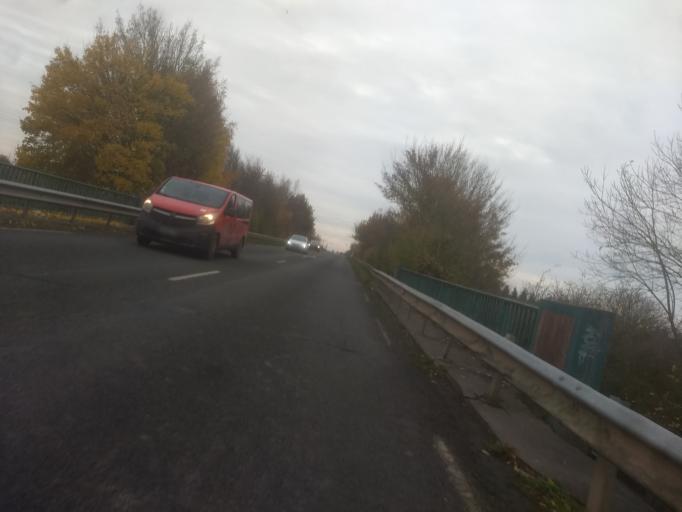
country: FR
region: Nord-Pas-de-Calais
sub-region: Departement du Pas-de-Calais
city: Achicourt
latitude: 50.2751
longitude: 2.7436
